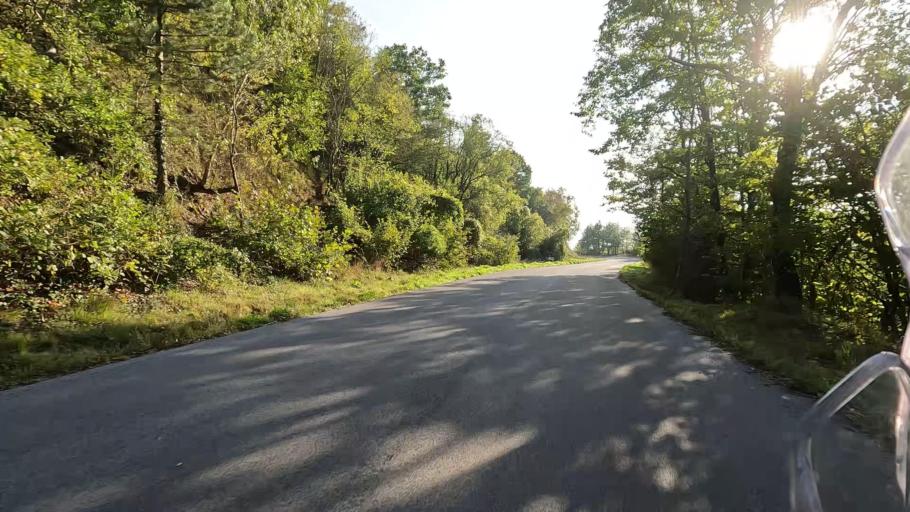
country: IT
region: Liguria
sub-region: Provincia di Savona
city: San Giovanni
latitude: 44.4166
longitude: 8.5295
